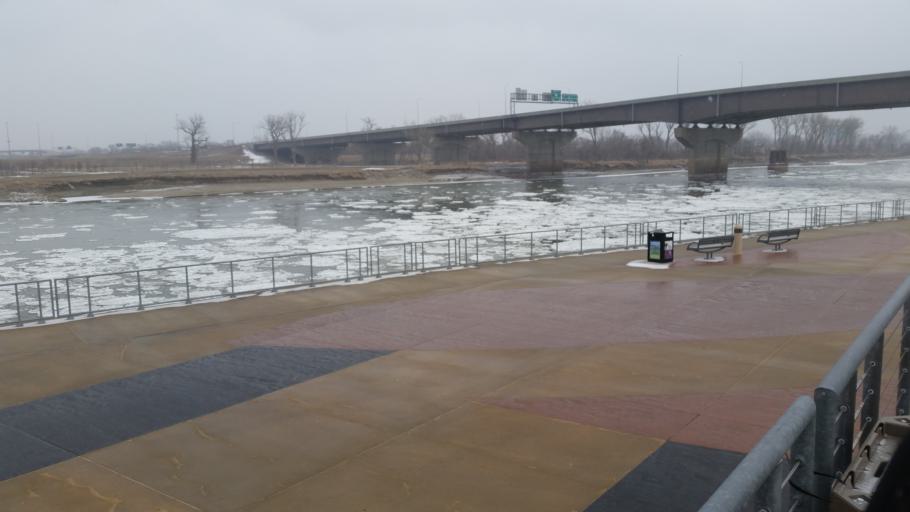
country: US
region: Nebraska
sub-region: Douglas County
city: Omaha
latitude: 41.2615
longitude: -95.9235
